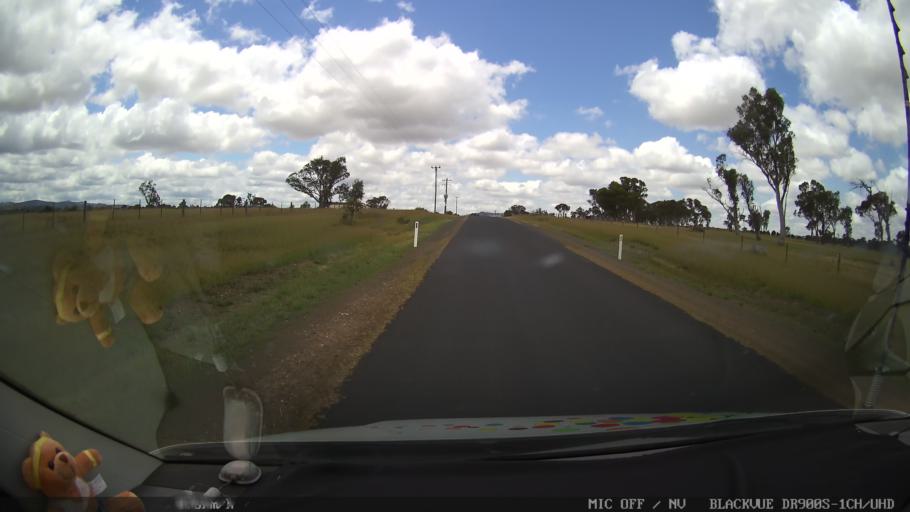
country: AU
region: New South Wales
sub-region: Glen Innes Severn
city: Glen Innes
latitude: -29.4428
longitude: 151.8377
